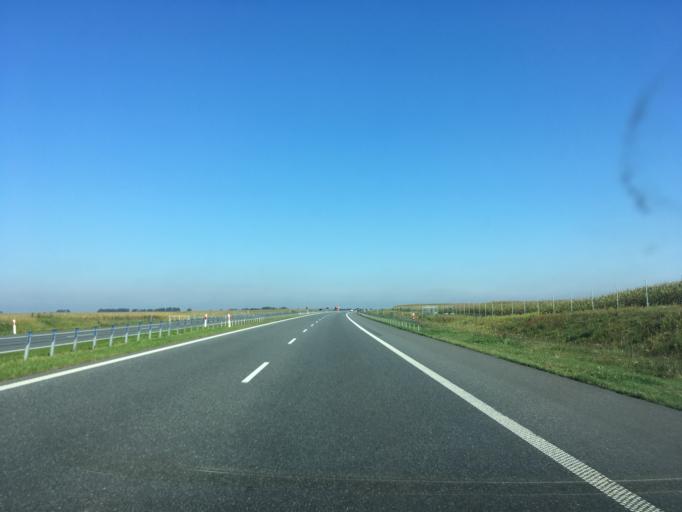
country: PL
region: Kujawsko-Pomorskie
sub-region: Powiat wabrzeski
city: Pluznica
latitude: 53.1803
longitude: 18.7377
